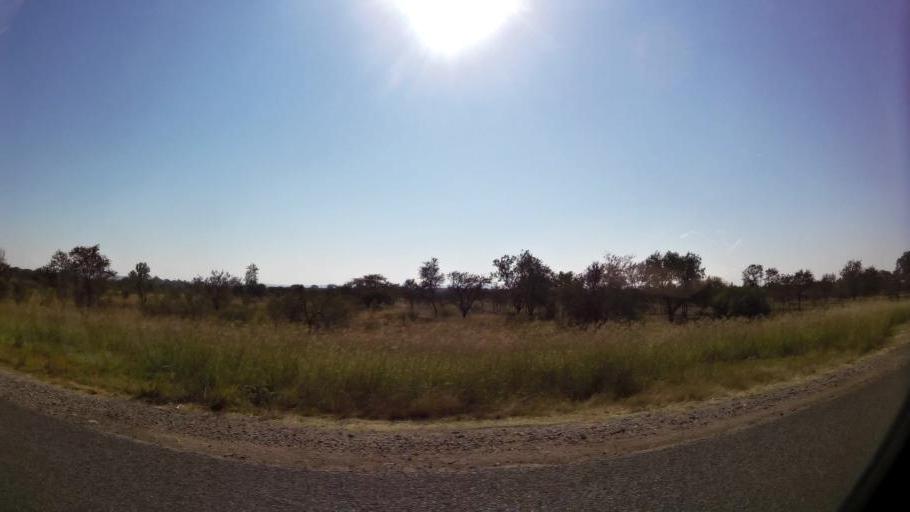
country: ZA
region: North-West
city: Ga-Rankuwa
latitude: -25.6576
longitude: 28.0632
